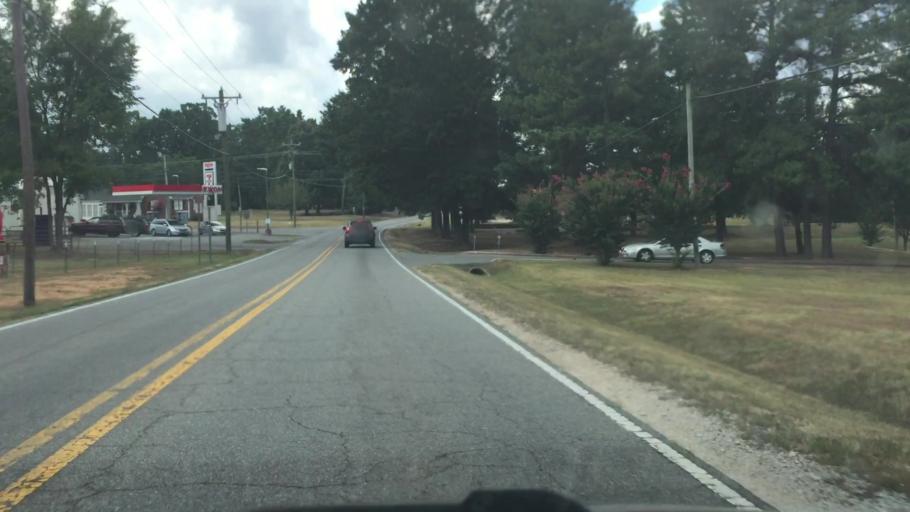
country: US
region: North Carolina
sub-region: Rowan County
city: Enochville
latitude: 35.5175
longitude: -80.6701
